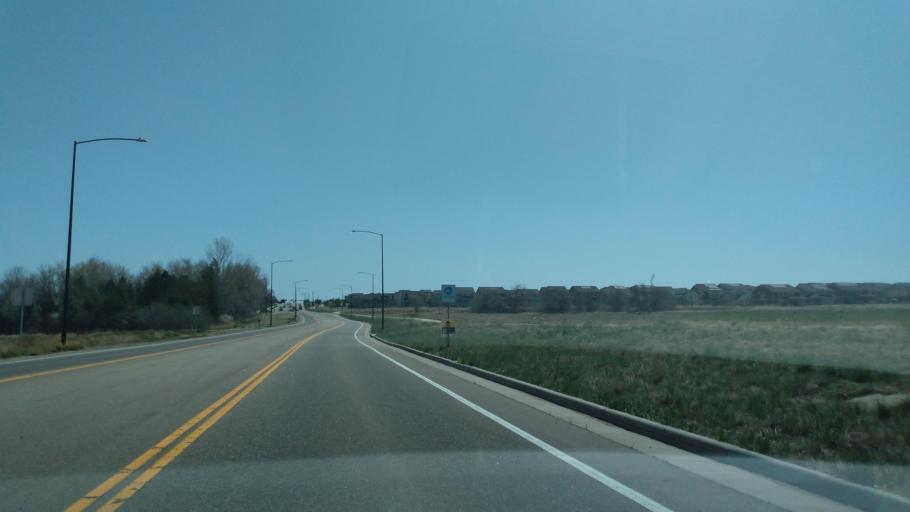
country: US
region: Colorado
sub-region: Boulder County
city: Lafayette
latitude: 40.0366
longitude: -105.0922
